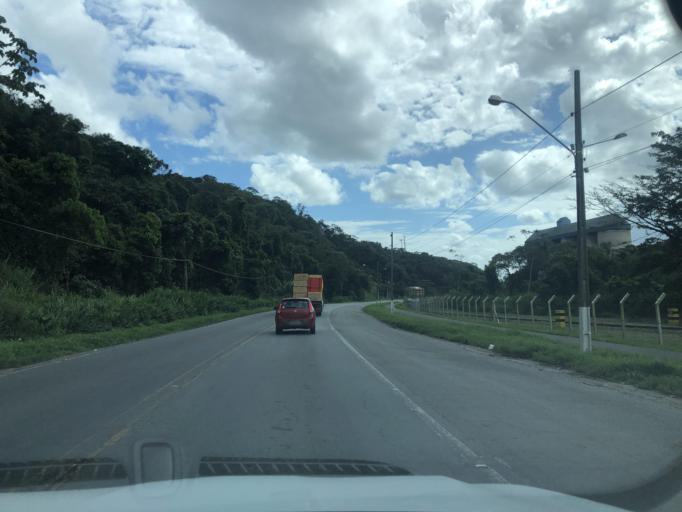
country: BR
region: Santa Catarina
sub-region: Sao Francisco Do Sul
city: Sao Francisco do Sul
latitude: -26.2379
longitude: -48.6301
